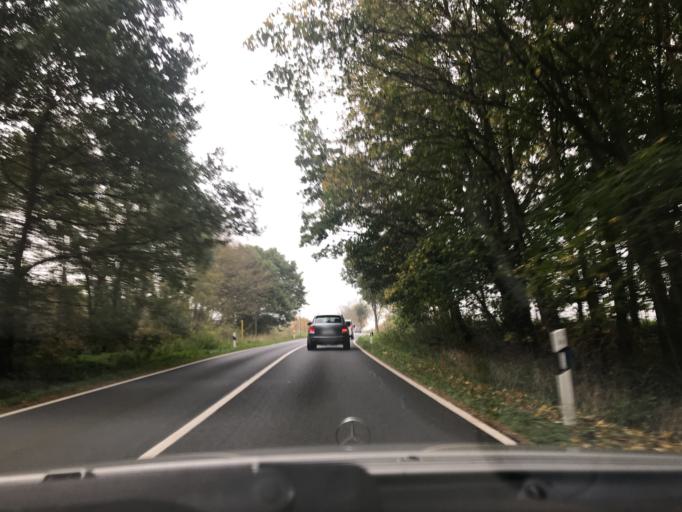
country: DE
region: Mecklenburg-Vorpommern
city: Wolgast
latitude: 54.0716
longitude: 13.7555
